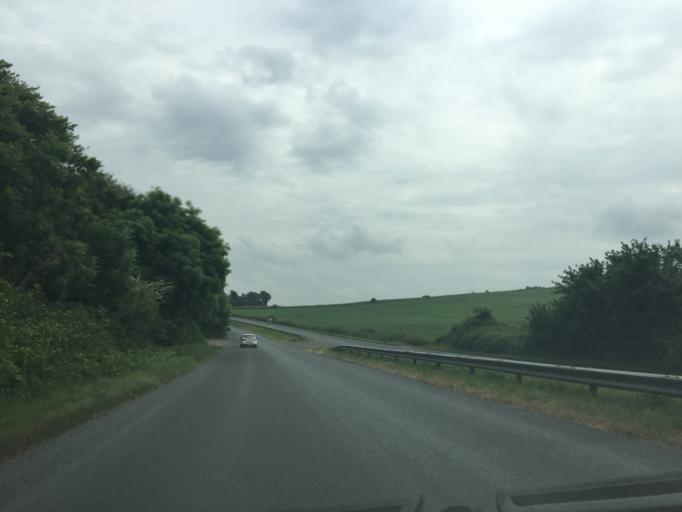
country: GB
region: England
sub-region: Dorset
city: Overcombe
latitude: 50.6642
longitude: -2.3387
